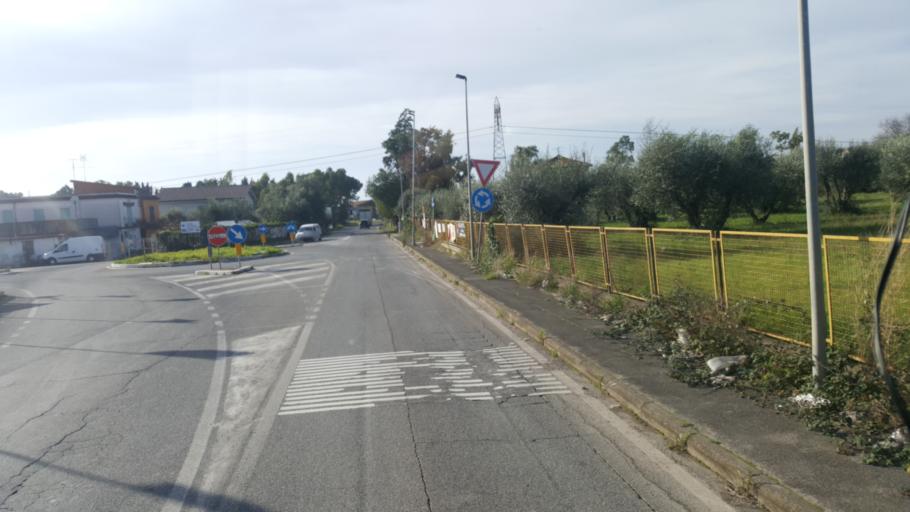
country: IT
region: Latium
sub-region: Provincia di Latina
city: Casalazzara
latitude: 41.6233
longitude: 12.5832
